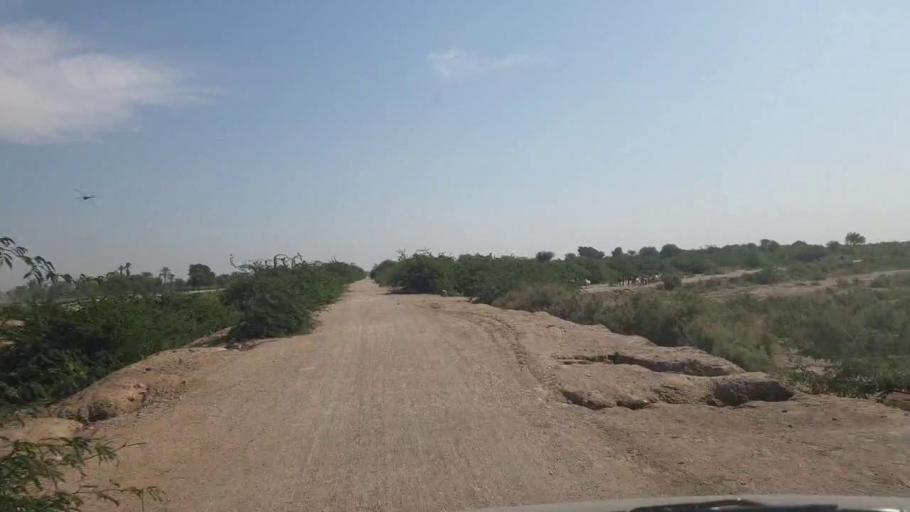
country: PK
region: Sindh
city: Digri
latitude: 24.9598
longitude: 69.1304
